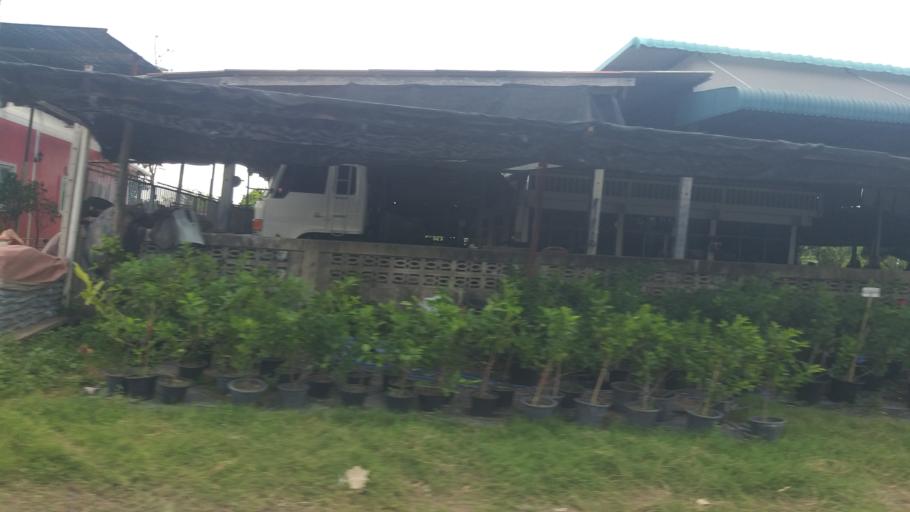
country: TH
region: Nakhon Nayok
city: Ban Na
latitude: 14.2994
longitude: 101.0694
